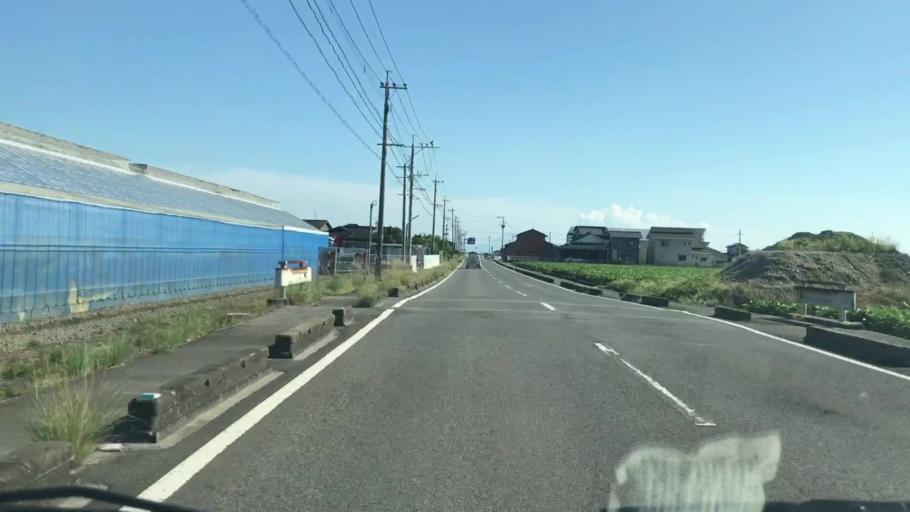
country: JP
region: Saga Prefecture
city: Okawa
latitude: 33.2010
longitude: 130.3351
